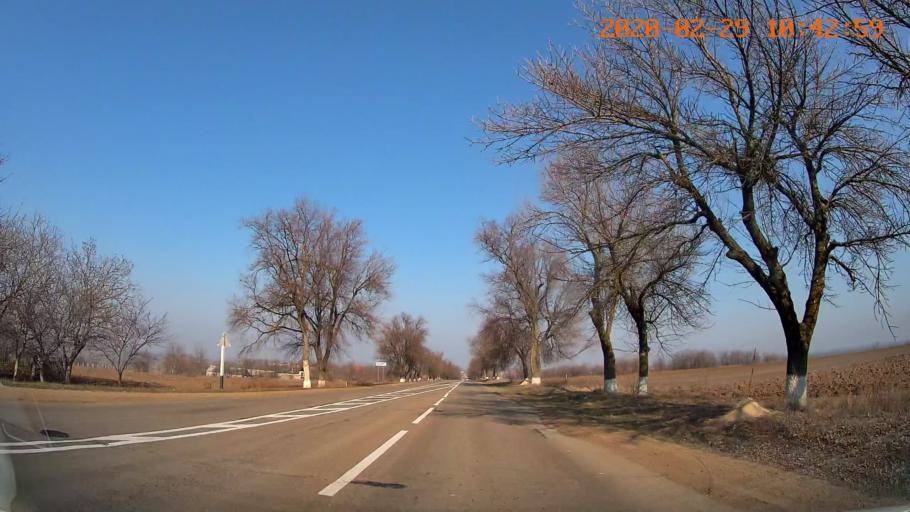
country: MD
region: Telenesti
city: Grigoriopol
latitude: 47.0563
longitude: 29.4056
